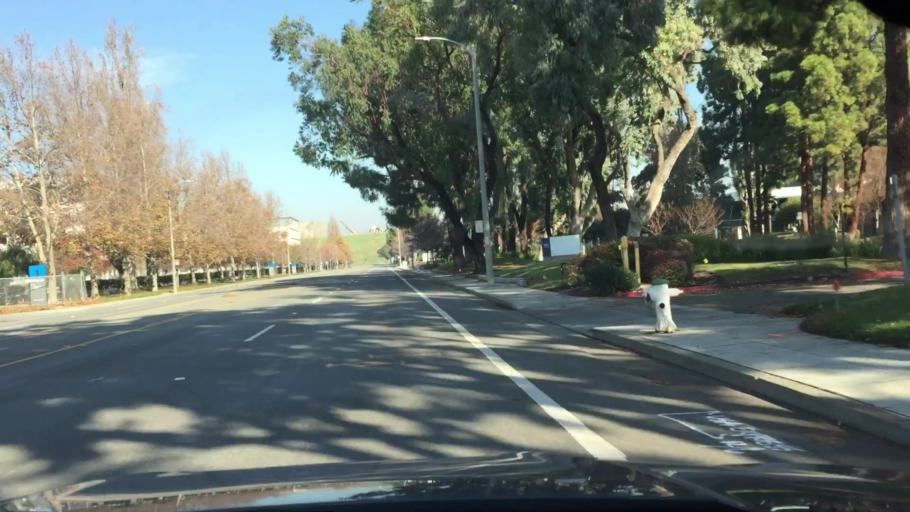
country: US
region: California
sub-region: Santa Clara County
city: Sunnyvale
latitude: 37.4106
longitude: -122.0102
